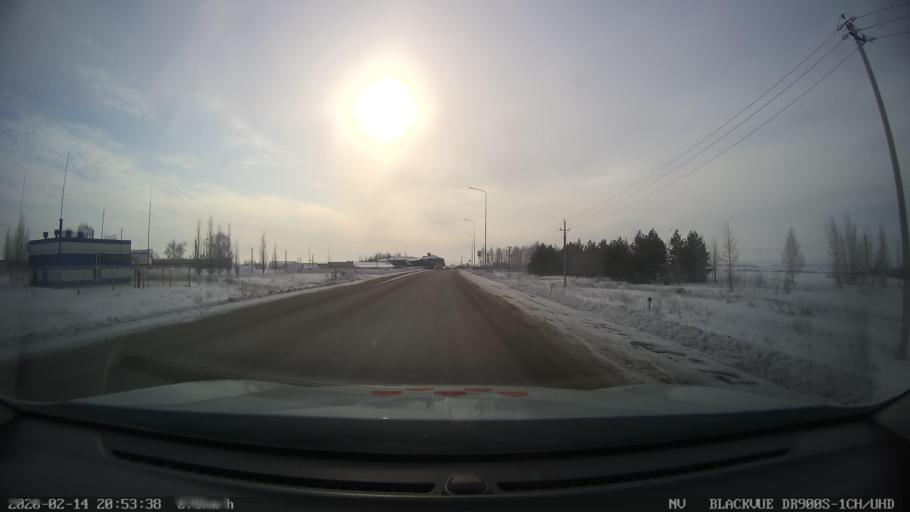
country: RU
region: Tatarstan
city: Kuybyshevskiy Zaton
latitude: 55.1925
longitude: 49.2475
